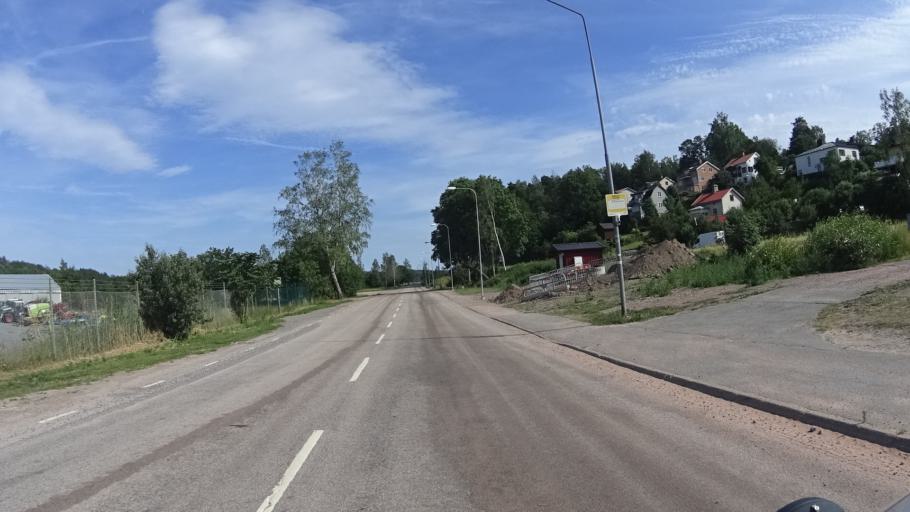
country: SE
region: Kalmar
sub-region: Vasterviks Kommun
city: Gamleby
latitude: 57.8970
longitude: 16.4104
